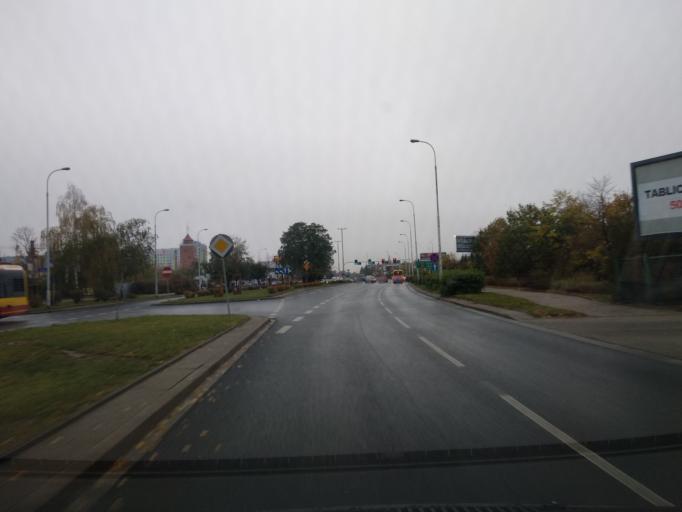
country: PL
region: Lower Silesian Voivodeship
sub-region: Powiat wroclawski
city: Wroclaw
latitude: 51.0848
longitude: 17.0351
